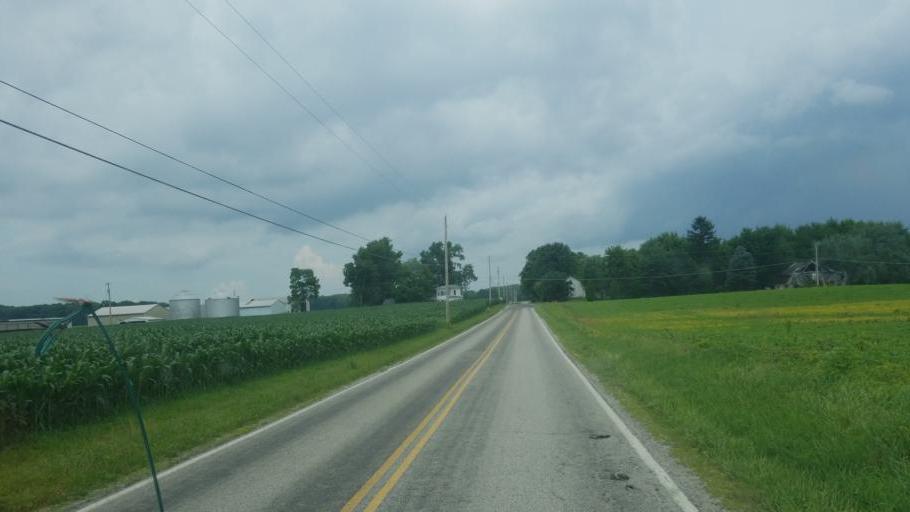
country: US
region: Ohio
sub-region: Wayne County
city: Wooster
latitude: 40.8931
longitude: -81.9534
